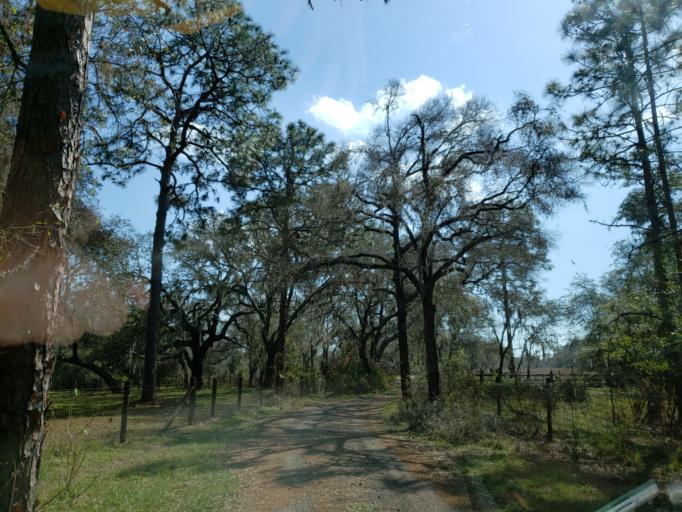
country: US
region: Florida
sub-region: Hillsborough County
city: Keystone
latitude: 28.1575
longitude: -82.6452
